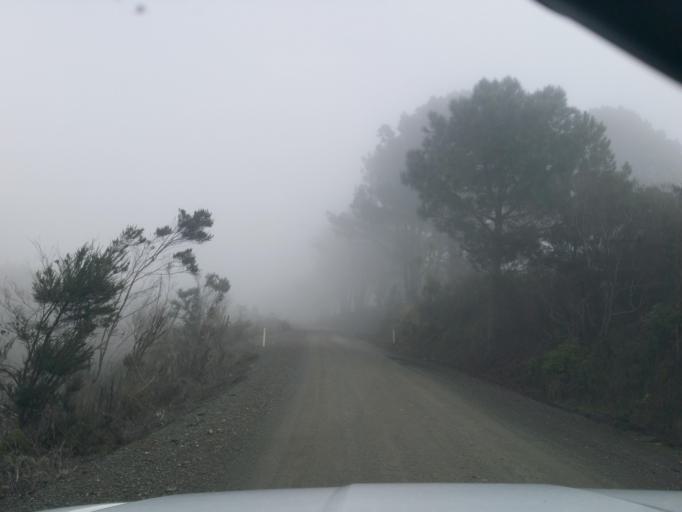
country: NZ
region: Northland
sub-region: Kaipara District
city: Dargaville
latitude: -35.9109
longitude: 173.7652
